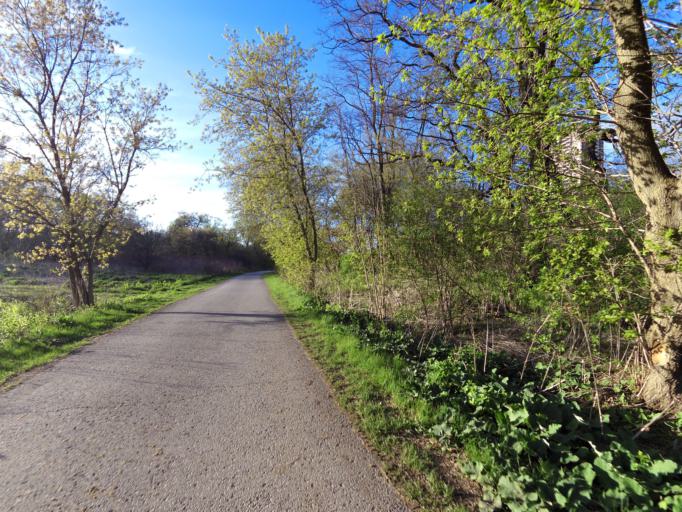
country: CA
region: Ontario
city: Toronto
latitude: 43.6768
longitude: -79.3633
